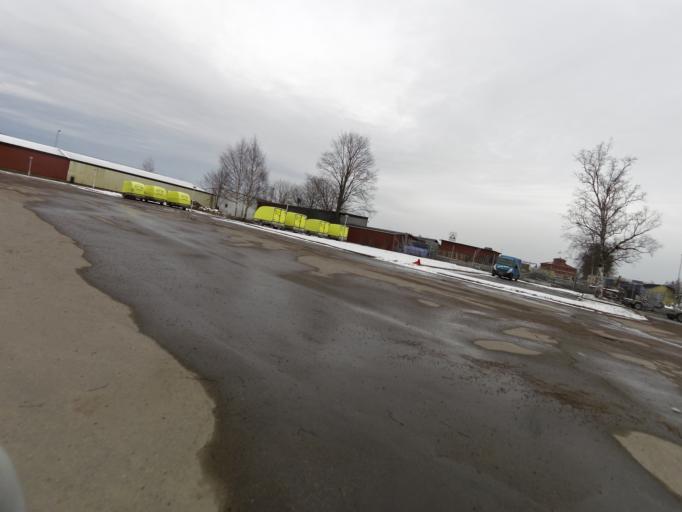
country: SE
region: Gaevleborg
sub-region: Gavle Kommun
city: Gavle
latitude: 60.6838
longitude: 17.1531
